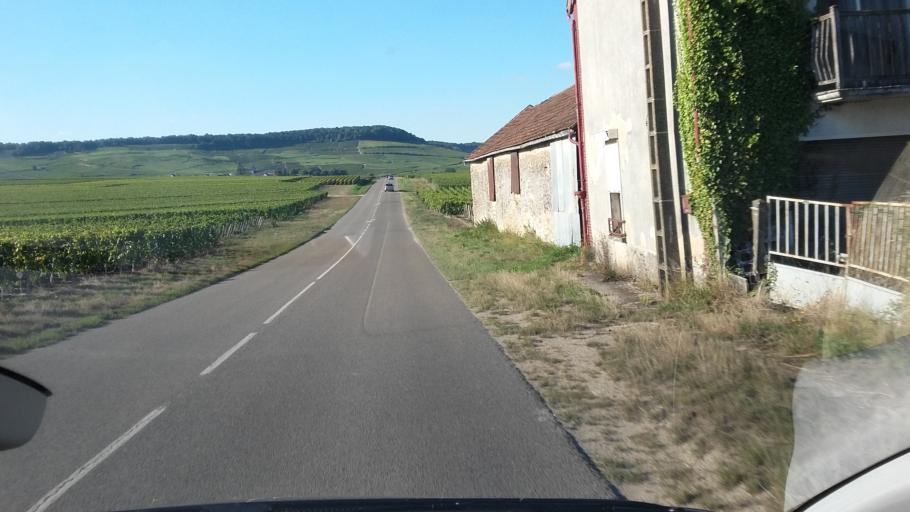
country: FR
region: Champagne-Ardenne
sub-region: Departement de la Marne
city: Le Mesnil-sur-Oger
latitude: 48.9514
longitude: 4.0229
